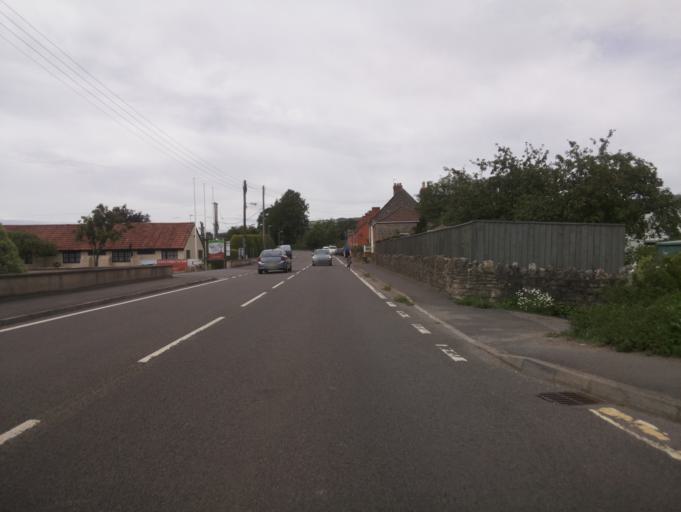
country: GB
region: England
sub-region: Somerset
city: Wells
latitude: 51.2110
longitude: -2.6720
